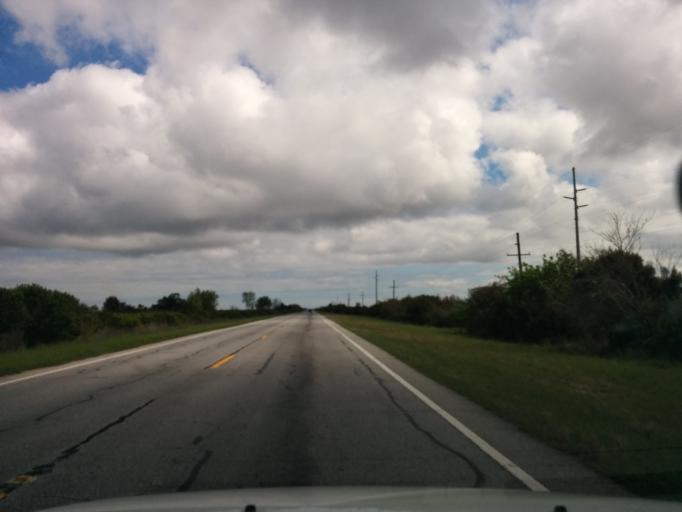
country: US
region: Georgia
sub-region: Glynn County
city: Brunswick
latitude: 31.0982
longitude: -81.4874
